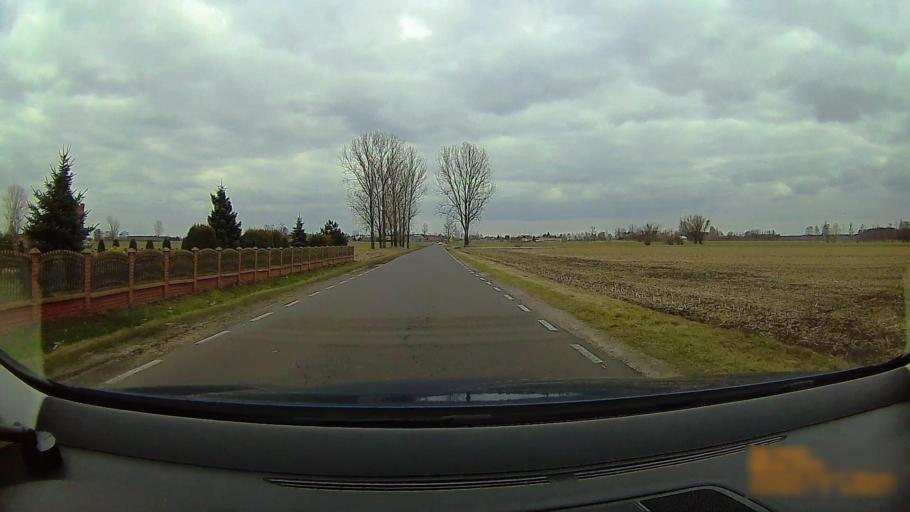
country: PL
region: Greater Poland Voivodeship
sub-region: Powiat koninski
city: Rzgow Pierwszy
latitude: 52.1091
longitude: 18.0793
